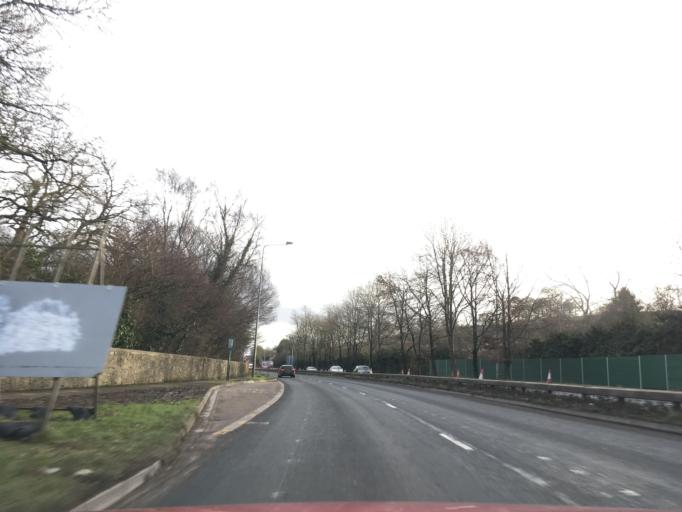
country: GB
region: Wales
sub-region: Newport
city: Newport
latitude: 51.5748
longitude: -3.0425
